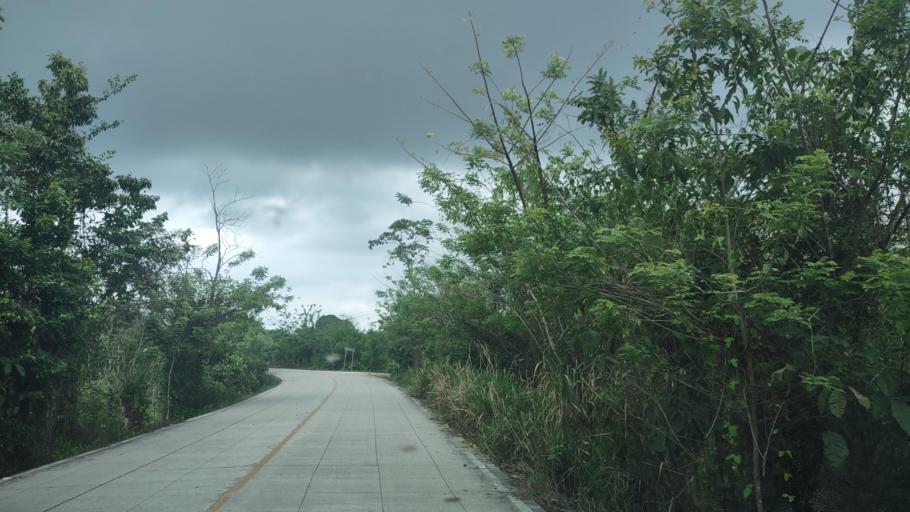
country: MX
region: Veracruz
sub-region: Uxpanapa
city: Poblado 10
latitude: 17.4933
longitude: -94.1789
